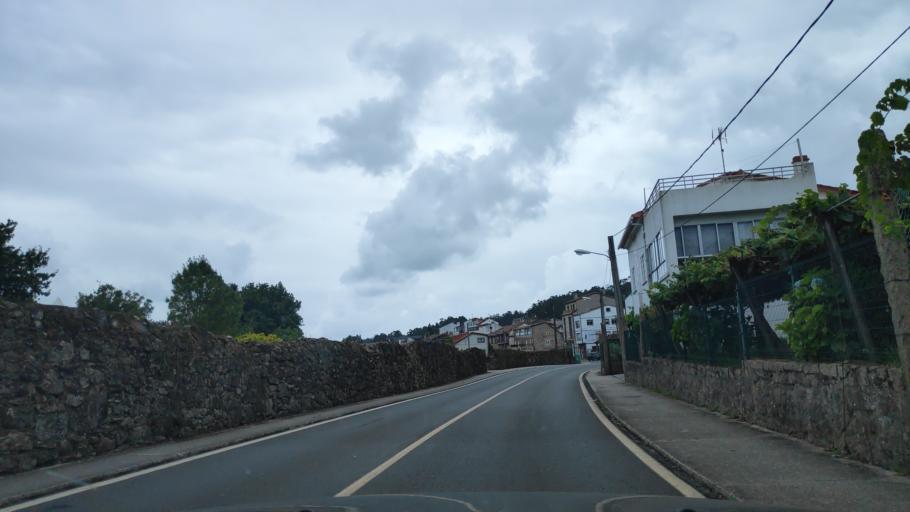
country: ES
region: Galicia
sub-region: Provincia da Coruna
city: Padron
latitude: 42.7333
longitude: -8.6671
